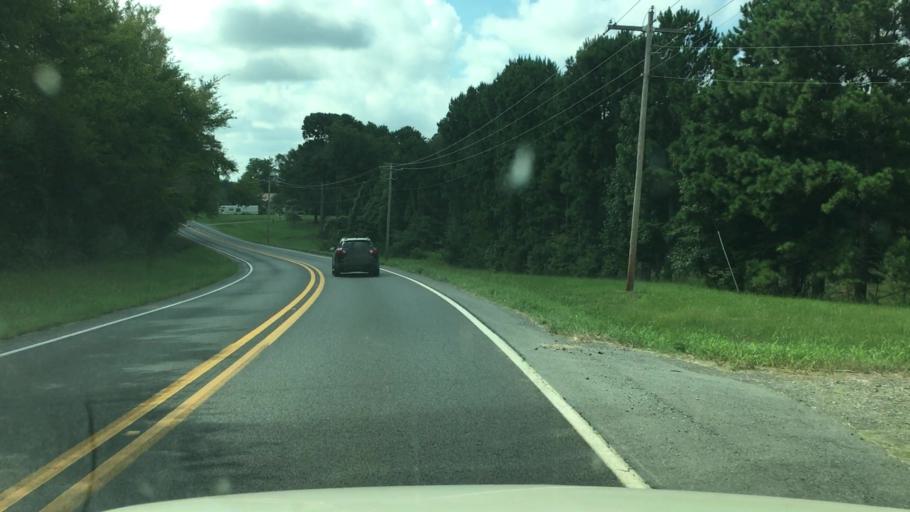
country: US
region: Arkansas
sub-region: Garland County
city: Lake Hamilton
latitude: 34.3035
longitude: -93.1665
